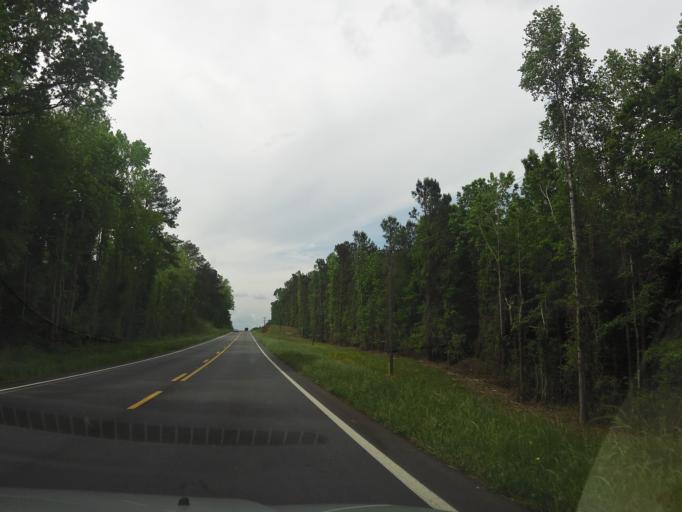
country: US
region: Georgia
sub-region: Jefferson County
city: Wrens
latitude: 33.3338
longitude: -82.4557
